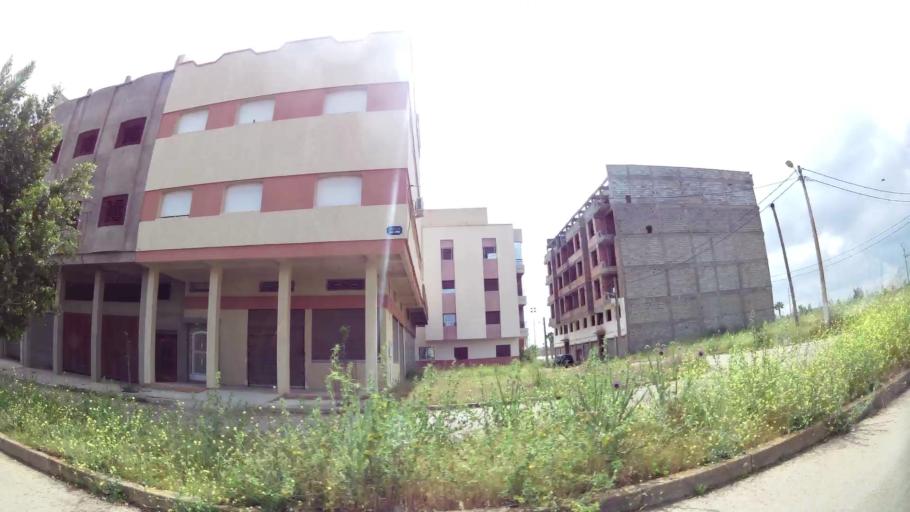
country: MA
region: Rabat-Sale-Zemmour-Zaer
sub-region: Khemisset
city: Tiflet
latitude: 33.8963
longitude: -6.3405
